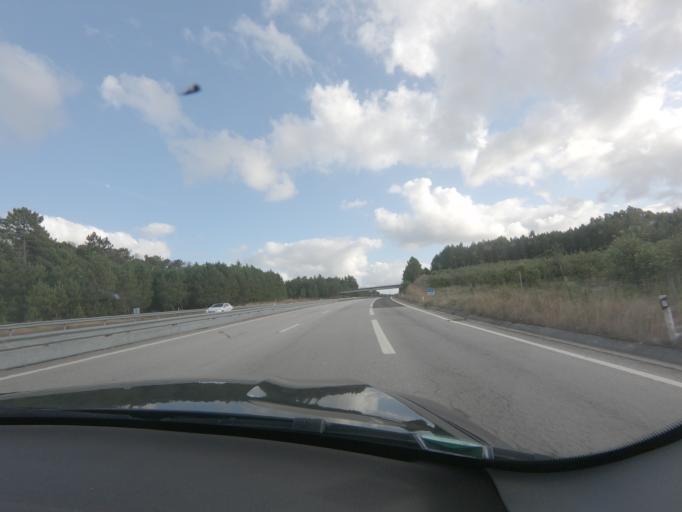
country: PT
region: Viseu
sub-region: Viseu
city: Campo
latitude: 40.7312
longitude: -7.9216
